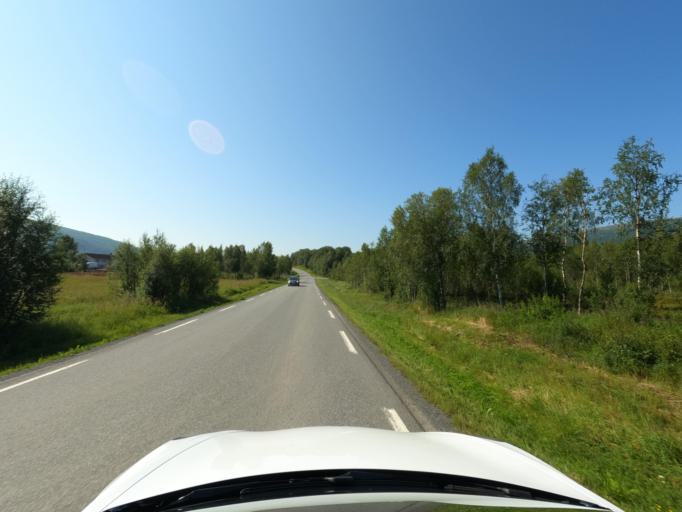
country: NO
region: Nordland
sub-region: Ballangen
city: Ballangen
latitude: 68.3486
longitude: 16.8517
